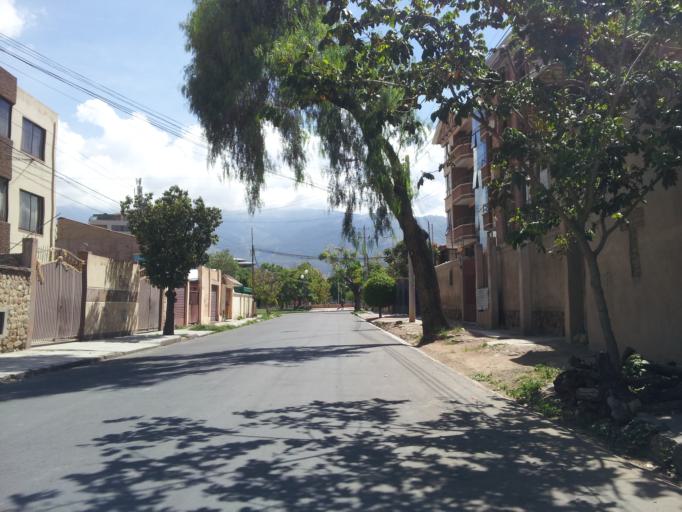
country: BO
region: Cochabamba
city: Cochabamba
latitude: -17.3862
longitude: -66.1739
